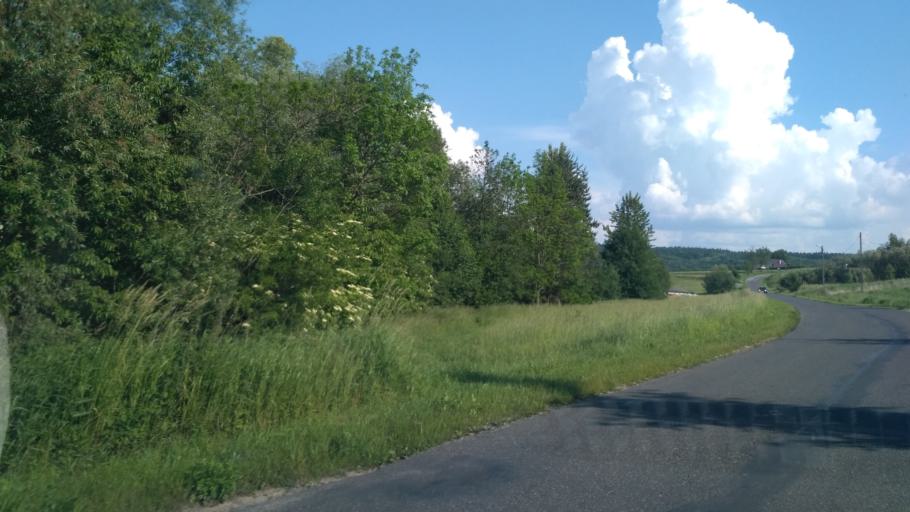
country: PL
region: Subcarpathian Voivodeship
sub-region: Powiat jaroslawski
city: Kramarzowka
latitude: 49.8724
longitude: 22.5104
